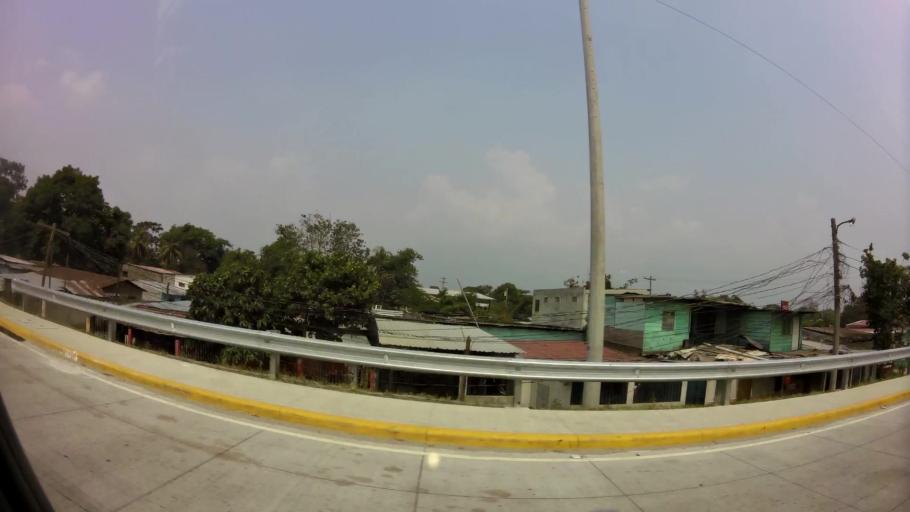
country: HN
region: Cortes
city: San Pedro Sula
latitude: 15.5124
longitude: -88.0029
